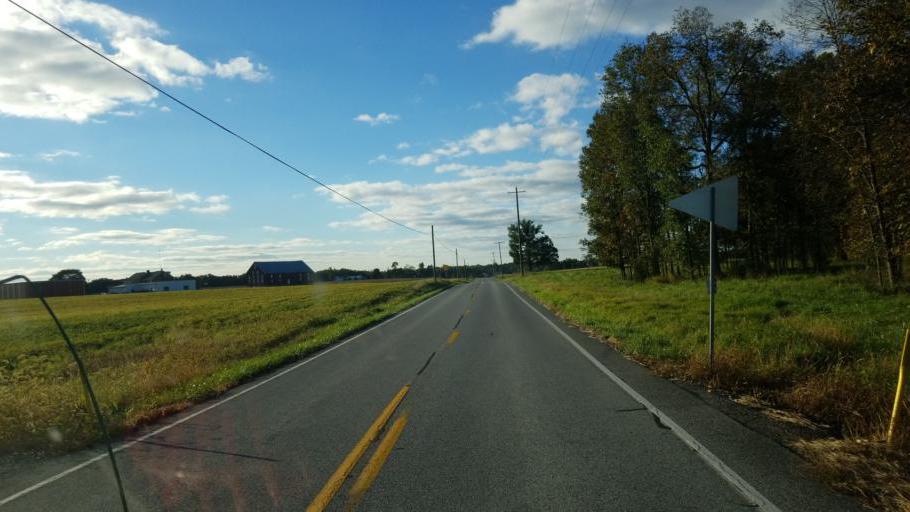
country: US
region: Pennsylvania
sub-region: Adams County
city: Gettysburg
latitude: 39.8658
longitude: -77.2288
